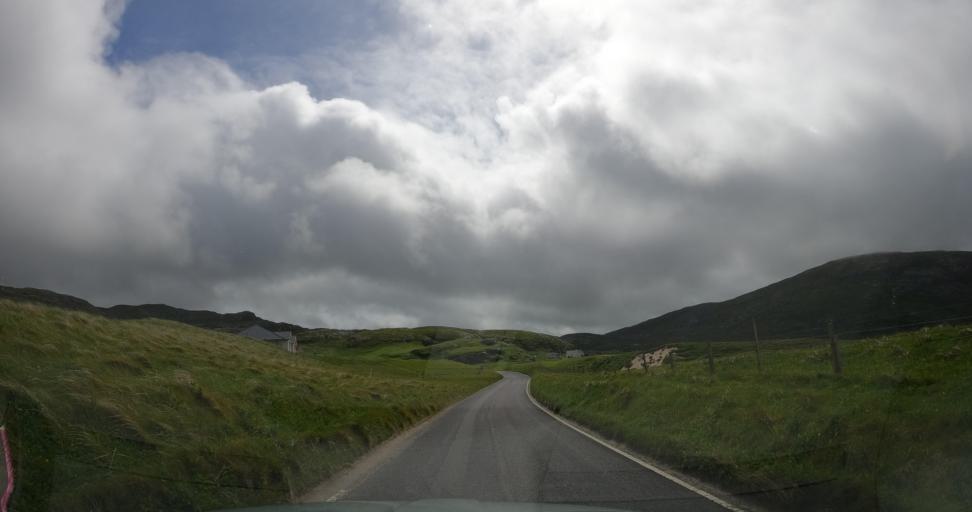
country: GB
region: Scotland
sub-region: Eilean Siar
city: Barra
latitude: 56.9743
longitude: -7.5167
